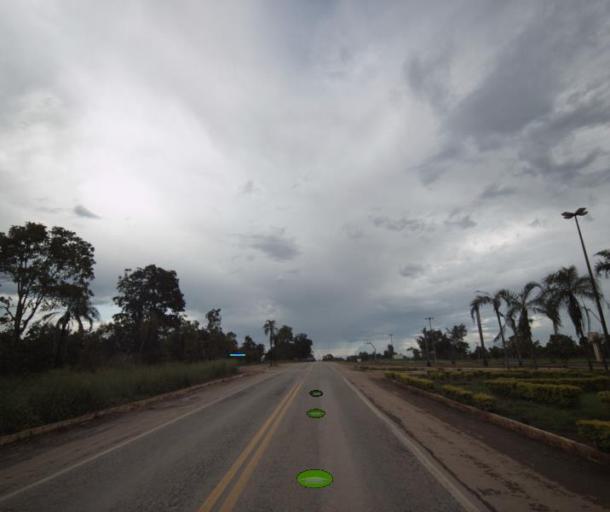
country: BR
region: Goias
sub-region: Porangatu
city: Porangatu
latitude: -13.5973
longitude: -49.0419
